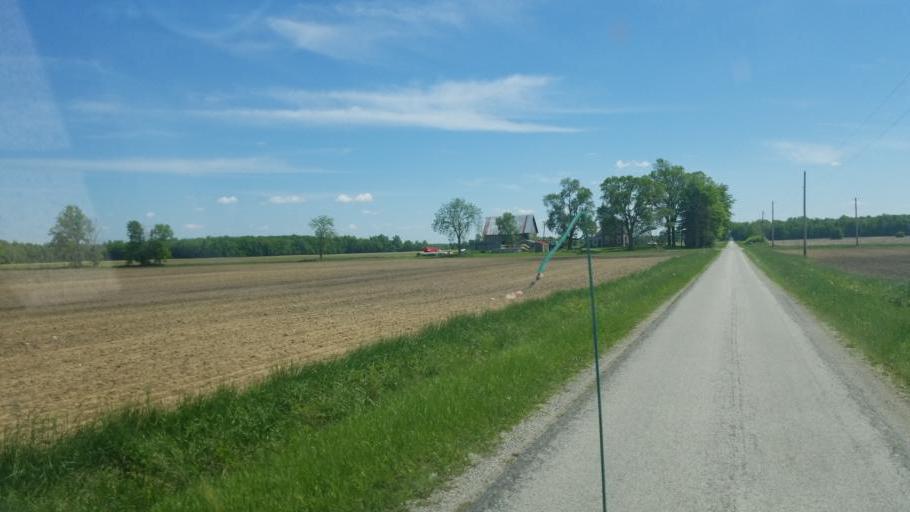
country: US
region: Ohio
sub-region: Huron County
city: Willard
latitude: 41.0534
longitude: -82.9390
